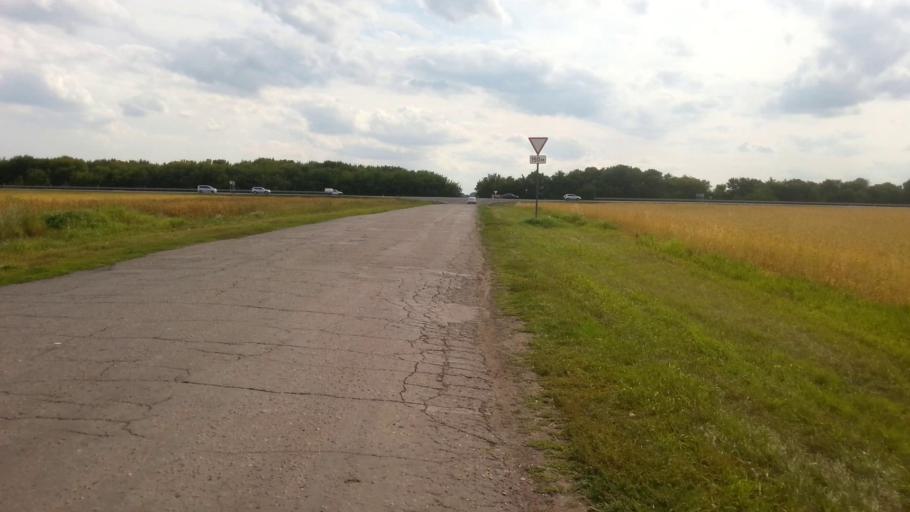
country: RU
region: Altai Krai
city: Nauchnyy Gorodok
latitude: 53.3584
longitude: 83.5084
